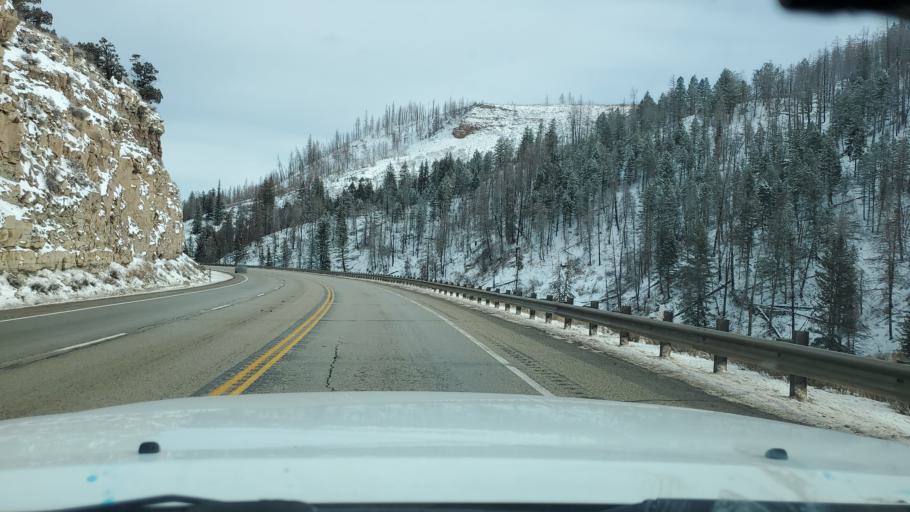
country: US
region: Utah
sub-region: Carbon County
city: Helper
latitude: 40.1940
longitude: -110.9361
